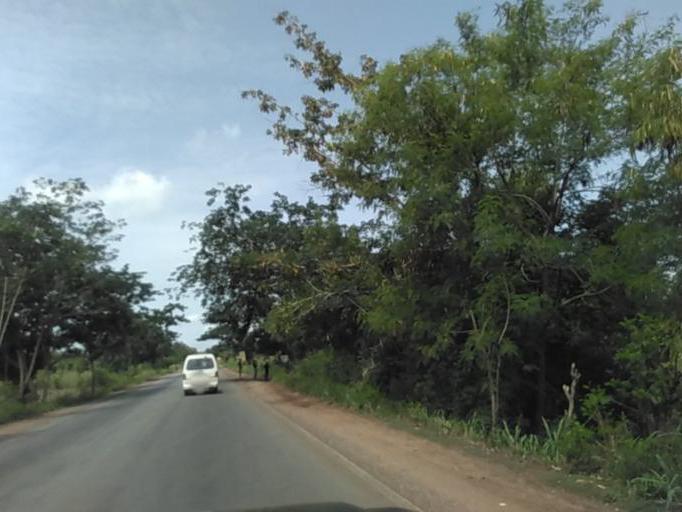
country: GH
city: Akropong
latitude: 6.1412
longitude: 0.0537
